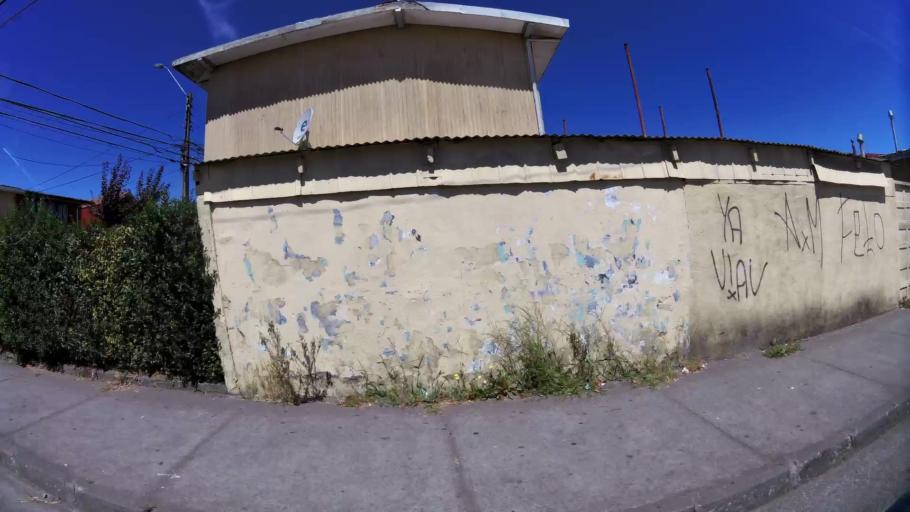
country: CL
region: Biobio
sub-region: Provincia de Concepcion
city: Talcahuano
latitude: -36.7579
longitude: -73.0930
